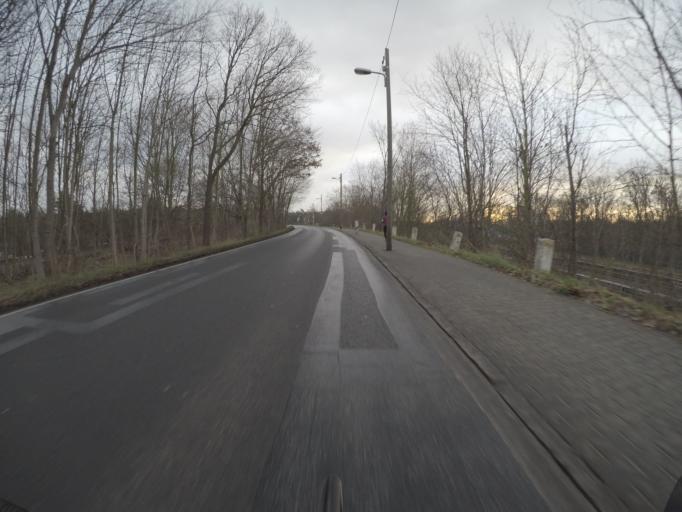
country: DE
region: Berlin
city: Karlshorst
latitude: 52.4701
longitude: 13.5512
